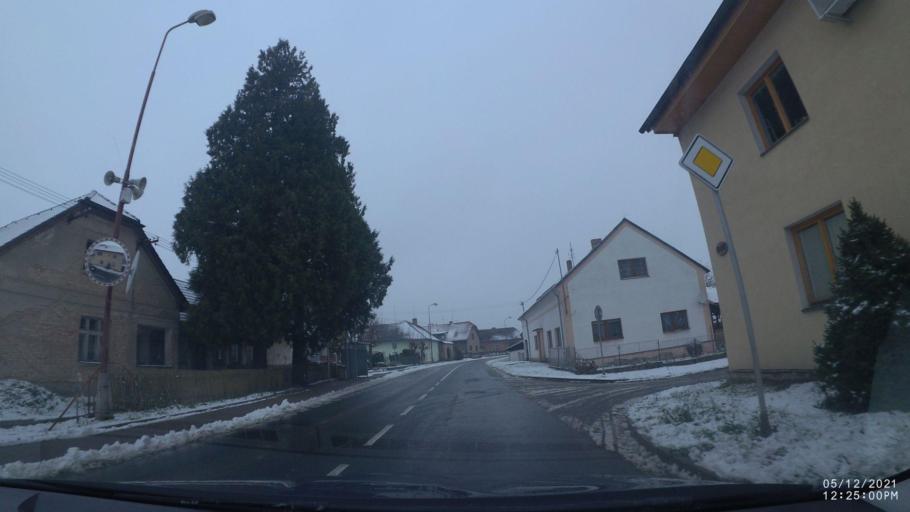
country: CZ
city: Ceske Mezirici
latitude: 50.3199
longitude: 16.0859
